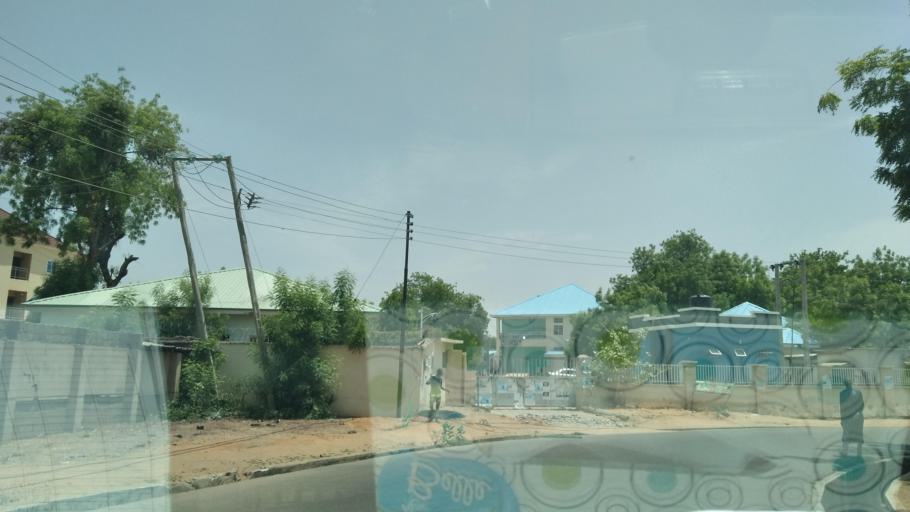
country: NG
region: Borno
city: Maiduguri
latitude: 11.8217
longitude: 13.1486
